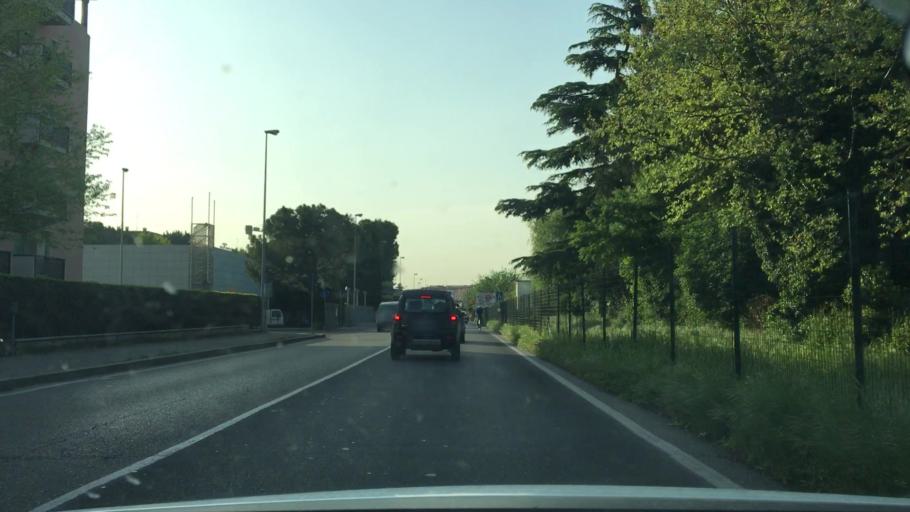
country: IT
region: Veneto
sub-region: Provincia di Verona
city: Verona
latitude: 45.4102
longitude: 11.0034
